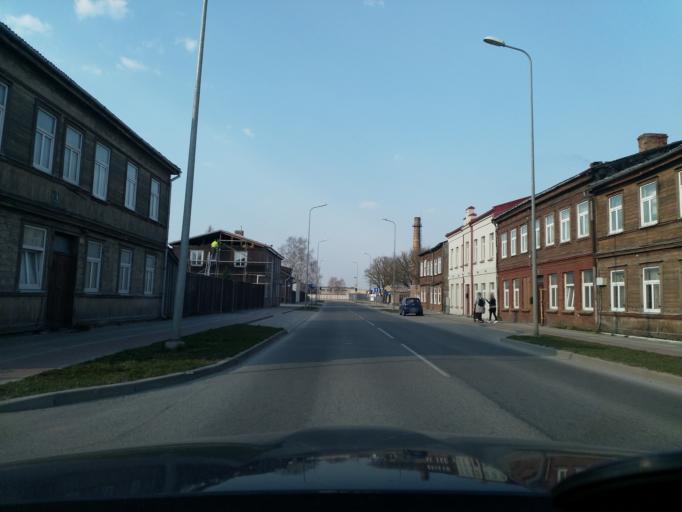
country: LV
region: Liepaja
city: Liepaja
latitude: 56.5079
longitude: 21.0254
